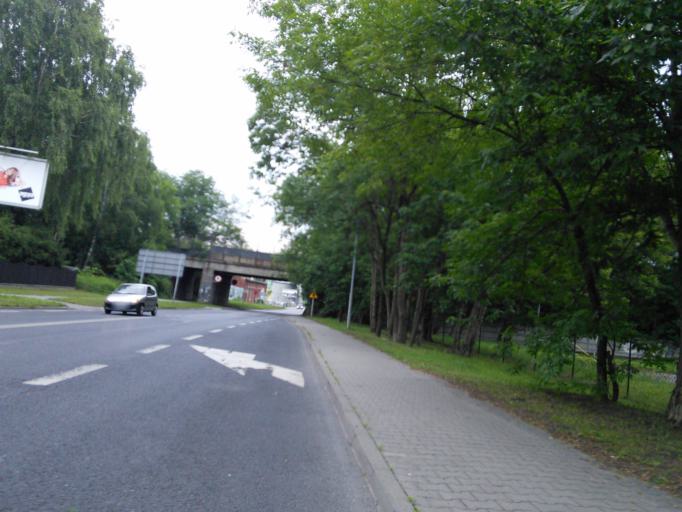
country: PL
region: Silesian Voivodeship
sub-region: Piekary Slaskie
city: Brzeziny Slaskie
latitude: 50.3712
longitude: 18.9563
